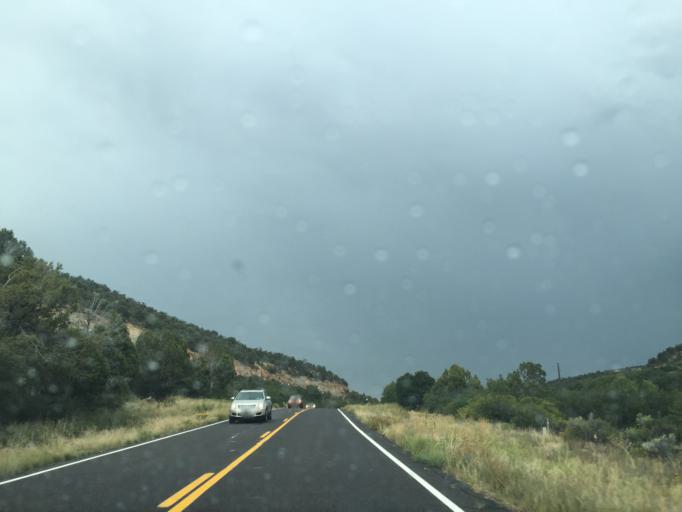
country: US
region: Utah
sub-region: Washington County
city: Hildale
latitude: 37.2376
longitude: -112.8521
